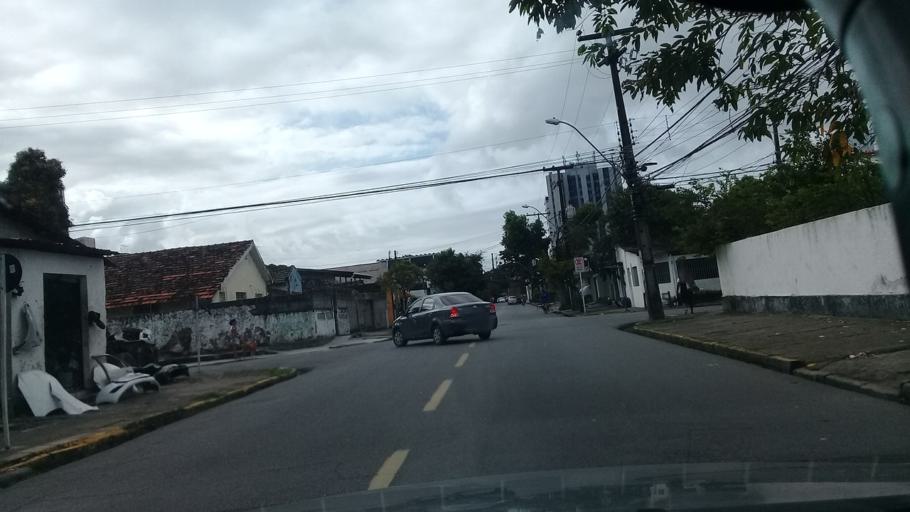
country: BR
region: Pernambuco
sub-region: Recife
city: Recife
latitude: -8.0341
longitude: -34.8809
